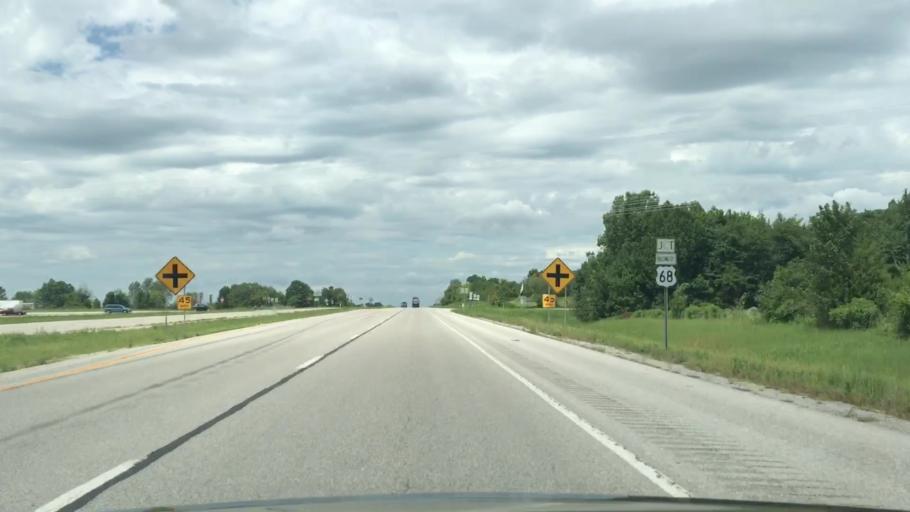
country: US
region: Kentucky
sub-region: Todd County
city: Elkton
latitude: 36.8226
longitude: -87.1976
